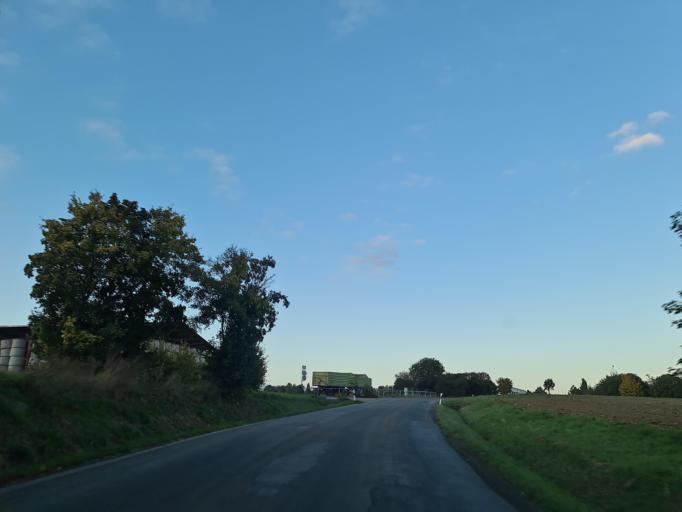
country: DE
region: Saxony
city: Syrau
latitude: 50.5295
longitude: 12.0977
